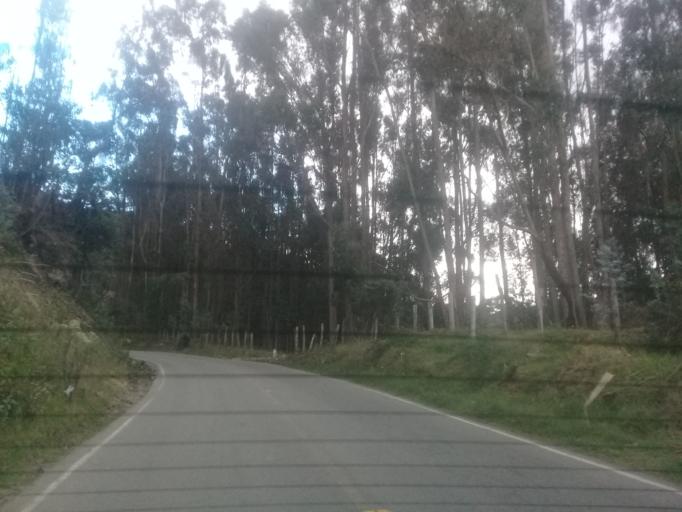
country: CO
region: Cundinamarca
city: Tabio
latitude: 4.9390
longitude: -74.1077
